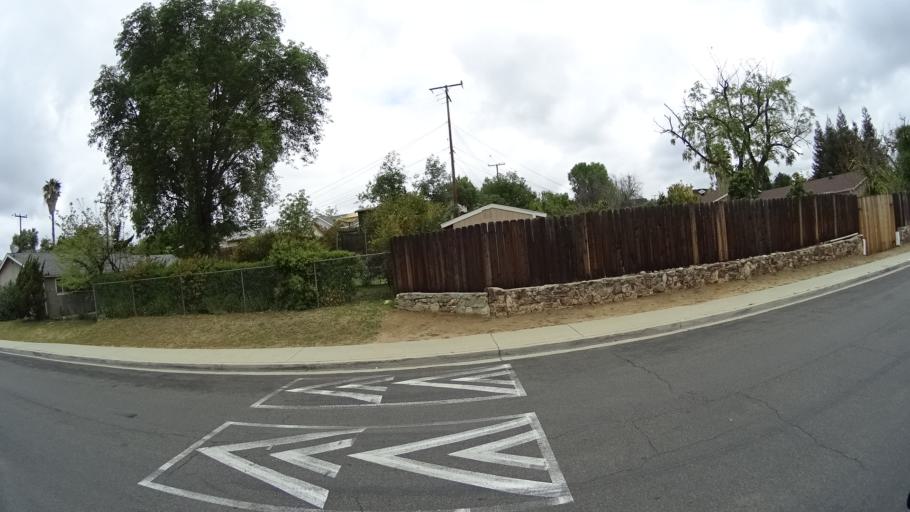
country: US
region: California
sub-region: Ventura County
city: Thousand Oaks
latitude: 34.2103
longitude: -118.8568
